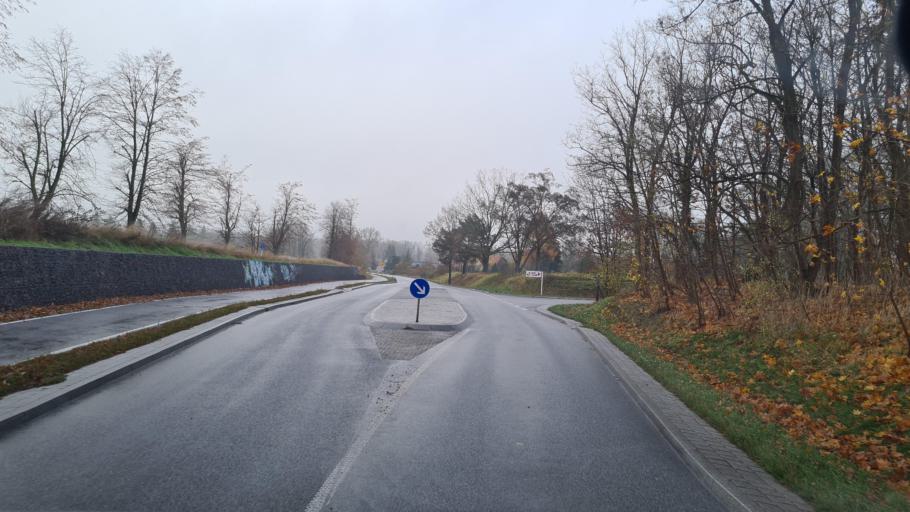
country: DE
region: Brandenburg
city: Gross Kreutz
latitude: 52.4001
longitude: 12.7706
